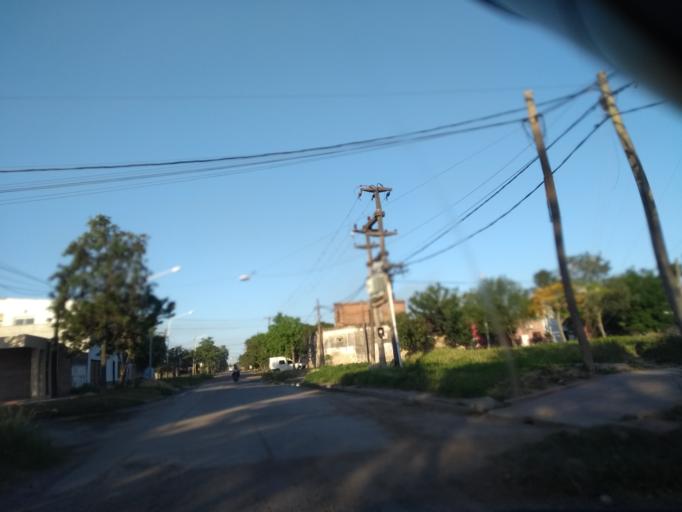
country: AR
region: Chaco
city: Barranqueras
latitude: -27.4863
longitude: -58.9401
